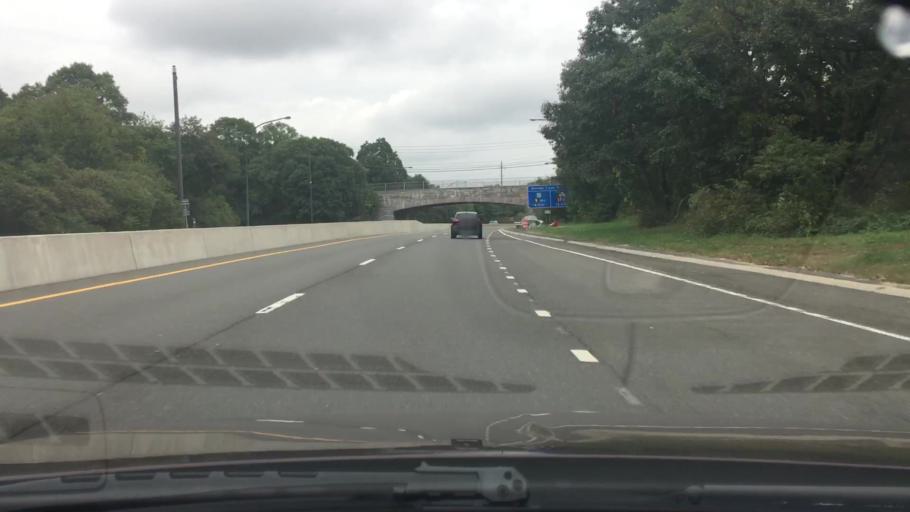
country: US
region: New York
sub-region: Suffolk County
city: Melville
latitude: 40.7985
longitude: -73.4061
